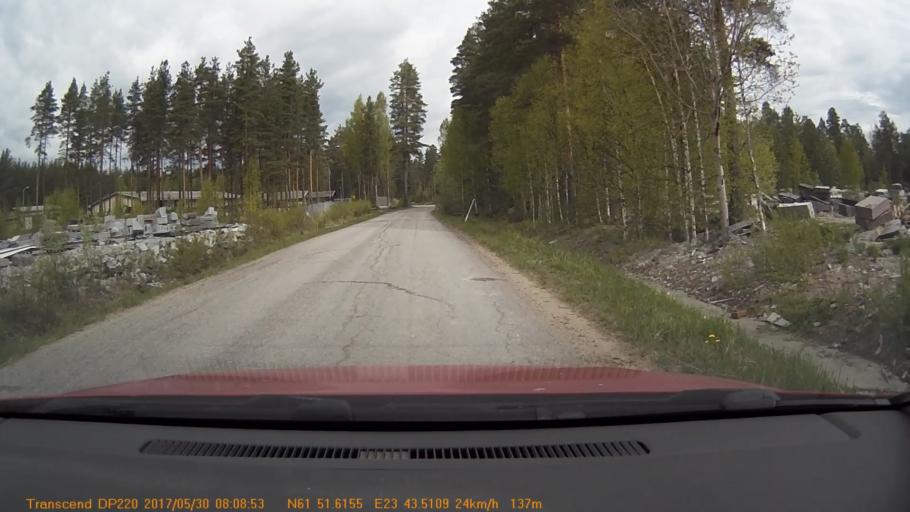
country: FI
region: Pirkanmaa
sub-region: Tampere
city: Kuru
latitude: 61.8602
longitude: 23.7251
